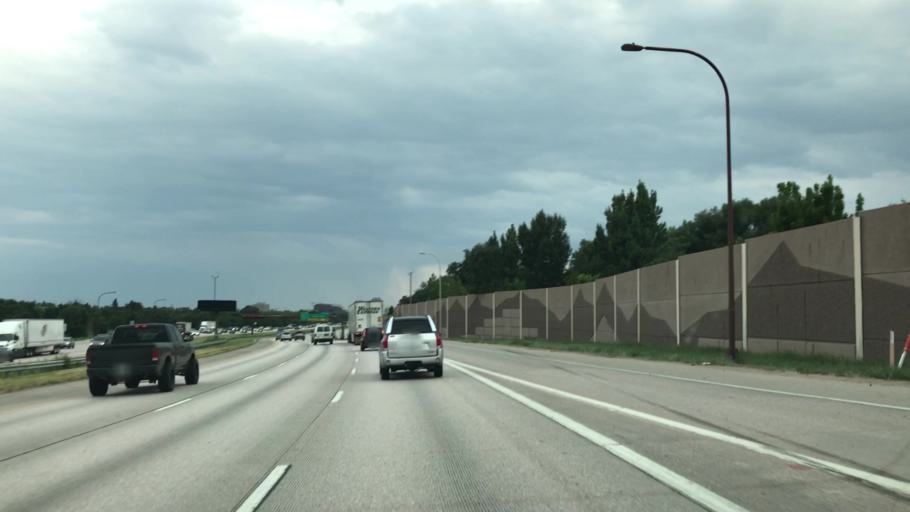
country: US
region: Colorado
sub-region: El Paso County
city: Colorado Springs
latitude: 38.8574
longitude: -104.8342
